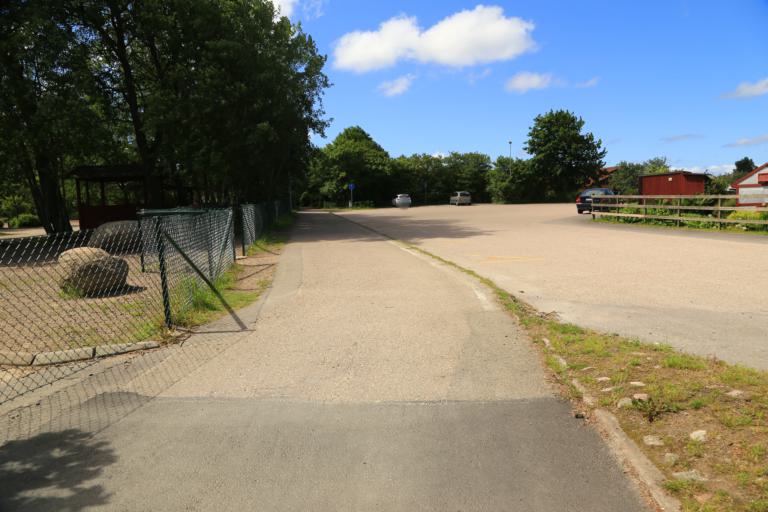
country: SE
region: Halland
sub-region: Varbergs Kommun
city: Varberg
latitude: 57.1159
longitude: 12.2880
